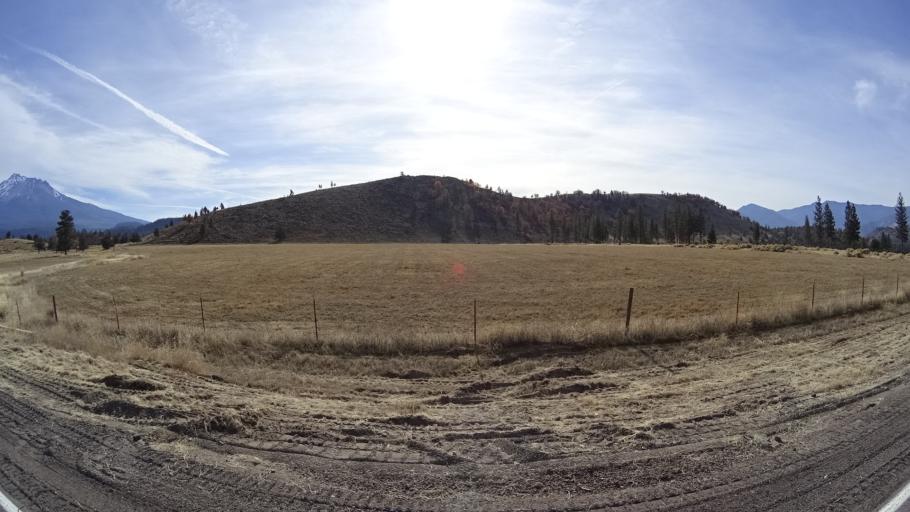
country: US
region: California
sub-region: Siskiyou County
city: Weed
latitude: 41.4941
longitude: -122.3940
